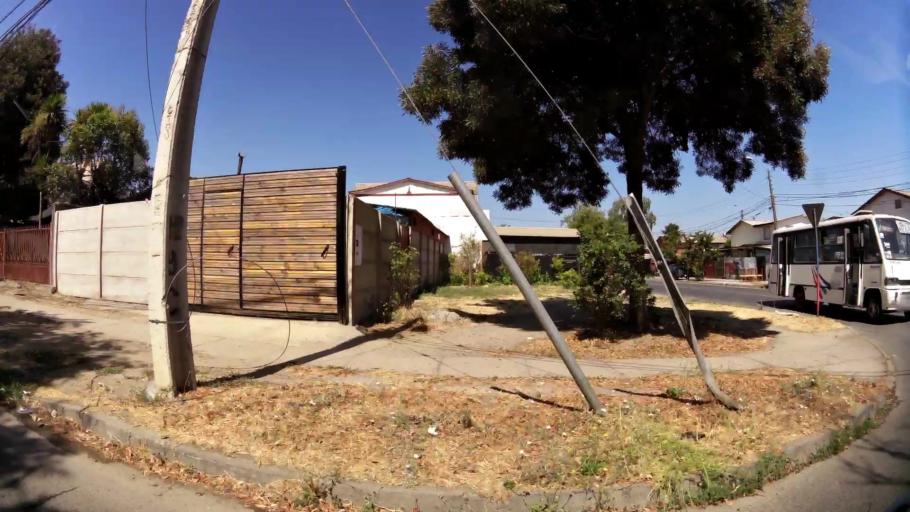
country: CL
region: Maule
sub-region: Provincia de Talca
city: Talca
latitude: -35.4152
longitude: -71.6397
